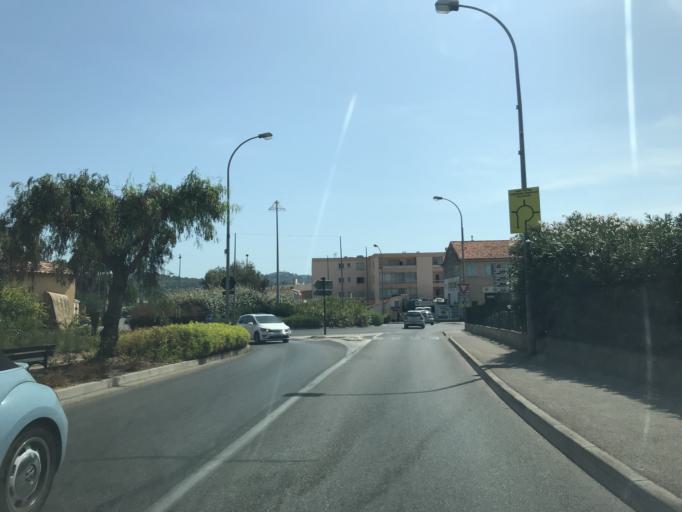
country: FR
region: Provence-Alpes-Cote d'Azur
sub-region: Departement du Var
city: Sanary-sur-Mer
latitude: 43.1219
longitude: 5.8046
